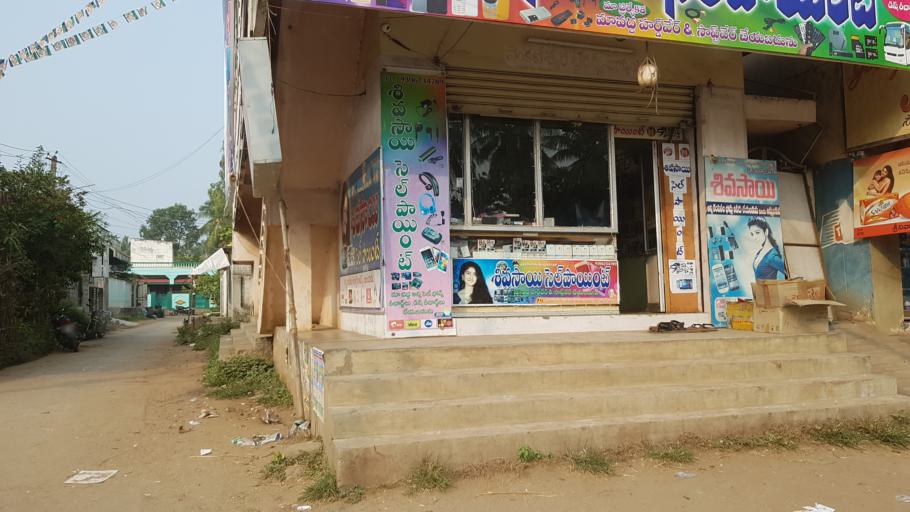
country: IN
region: Andhra Pradesh
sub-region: West Godavari
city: Akividu
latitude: 16.5368
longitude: 81.4134
